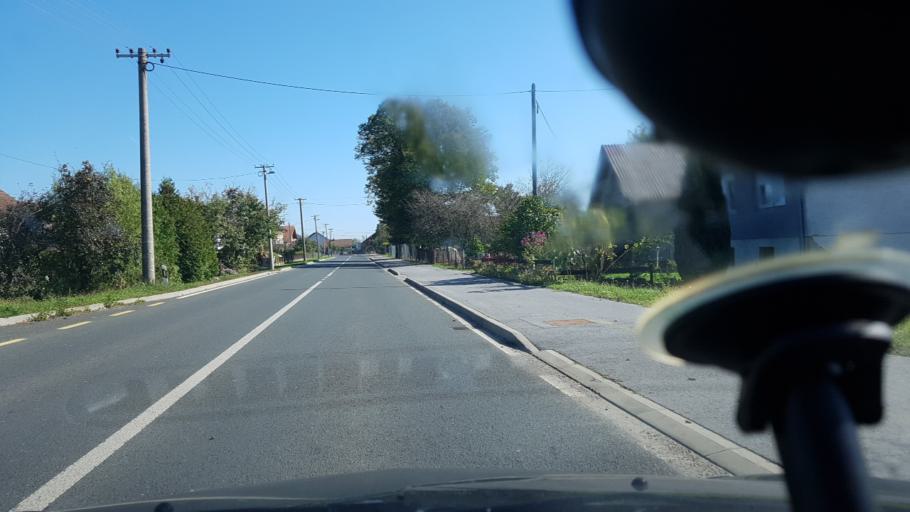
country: HR
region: Zagrebacka
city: Kriz
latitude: 45.7124
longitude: 16.4325
